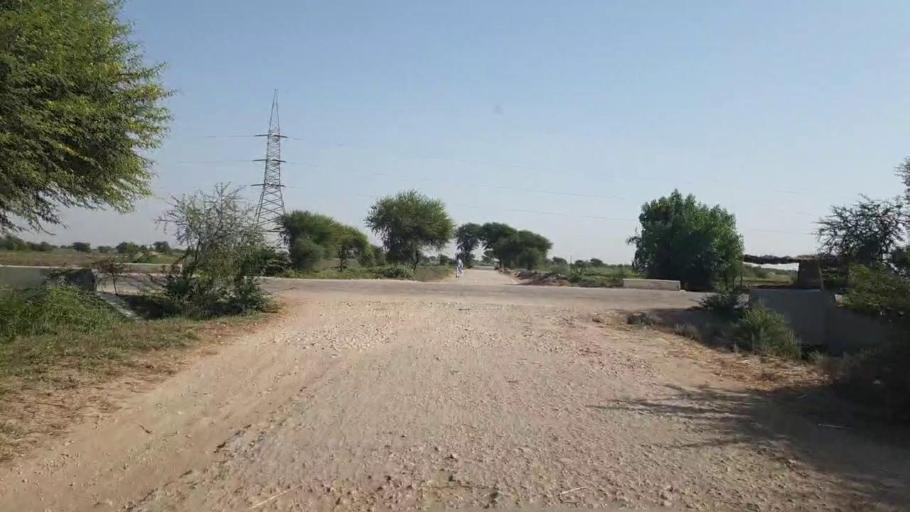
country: PK
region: Sindh
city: Matli
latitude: 25.0527
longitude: 68.7217
